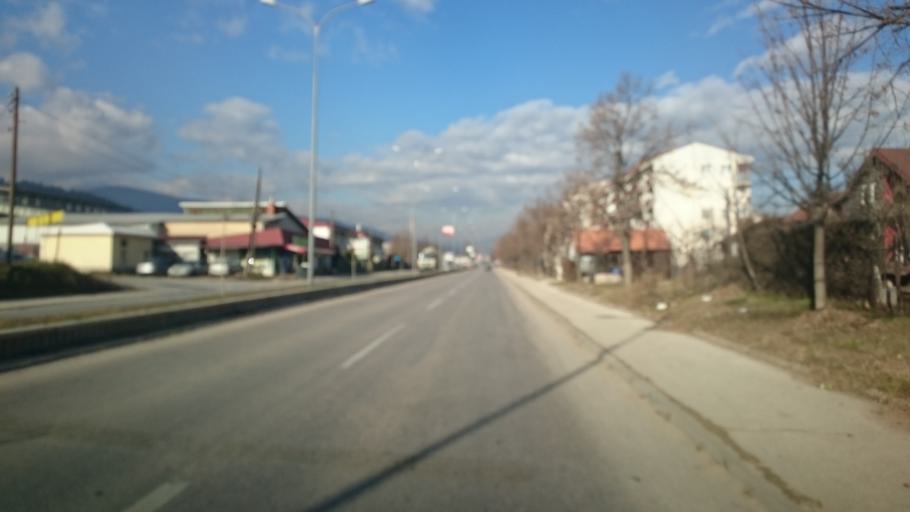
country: MK
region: Kicevo
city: Kicevo
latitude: 41.5095
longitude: 20.9525
